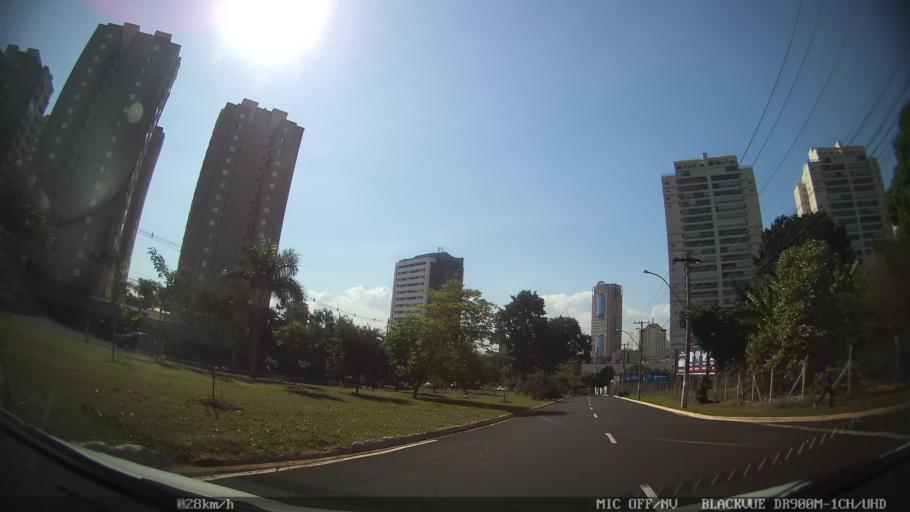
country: BR
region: Sao Paulo
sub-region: Ribeirao Preto
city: Ribeirao Preto
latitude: -21.2154
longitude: -47.8213
